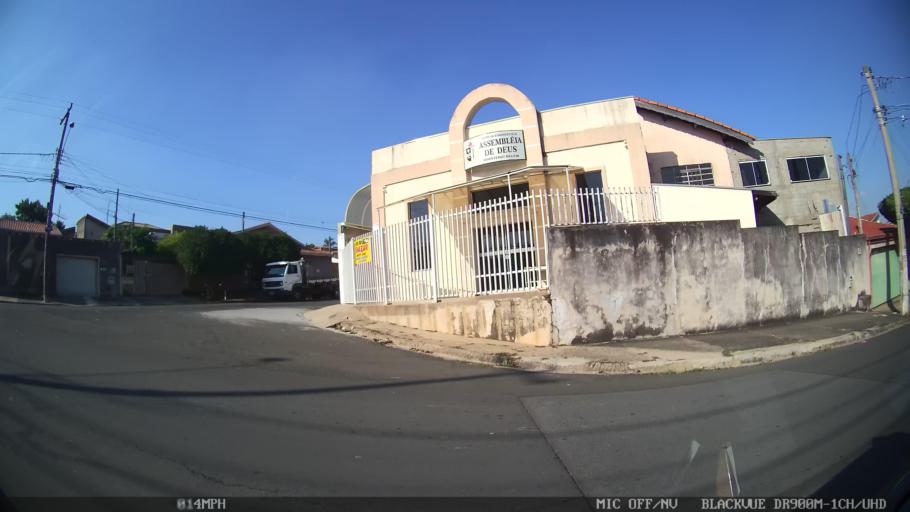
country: BR
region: Sao Paulo
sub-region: Indaiatuba
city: Indaiatuba
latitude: -22.9902
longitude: -47.1461
